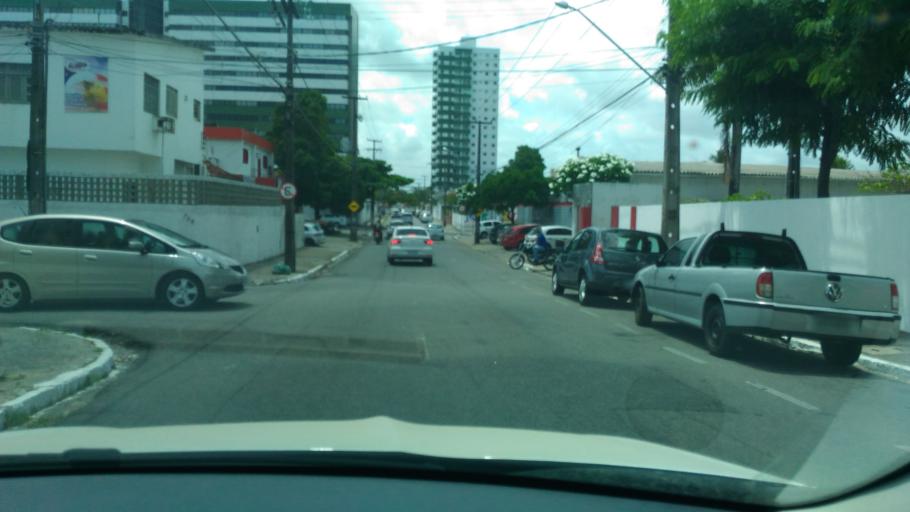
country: BR
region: Paraiba
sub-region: Joao Pessoa
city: Joao Pessoa
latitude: -7.1187
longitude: -34.8621
